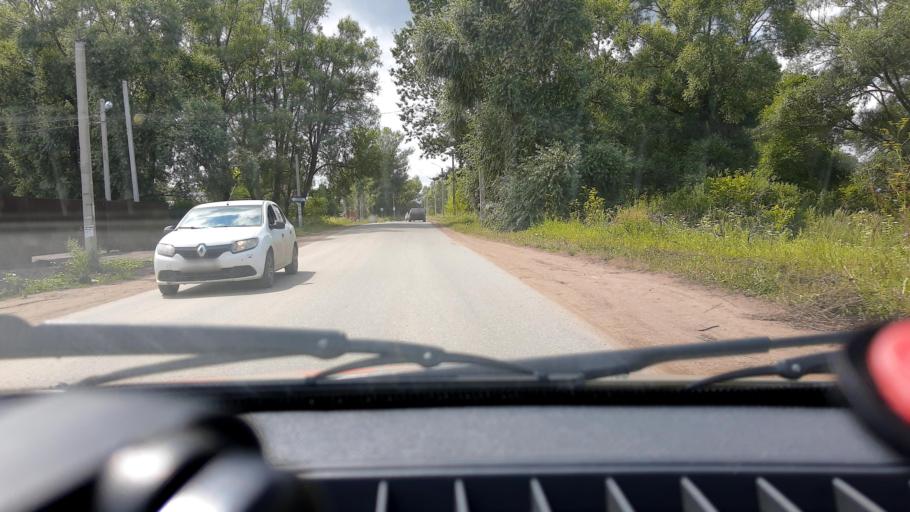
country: RU
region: Bashkortostan
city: Ufa
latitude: 54.6624
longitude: 56.0705
